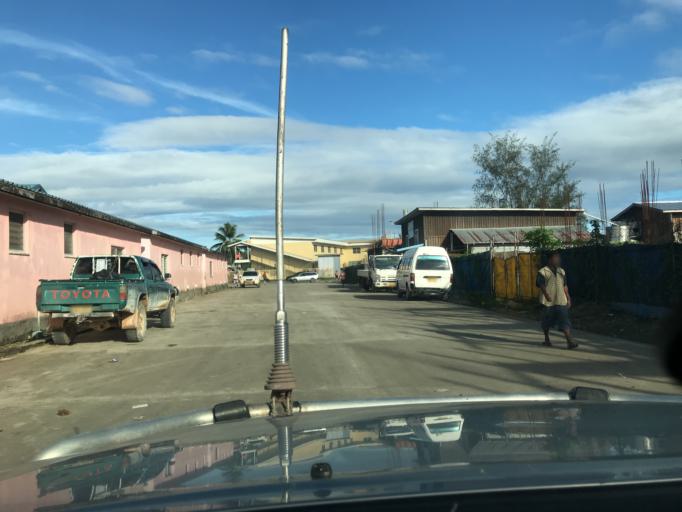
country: SB
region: Malaita
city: Auki
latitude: -8.7729
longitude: 160.6997
